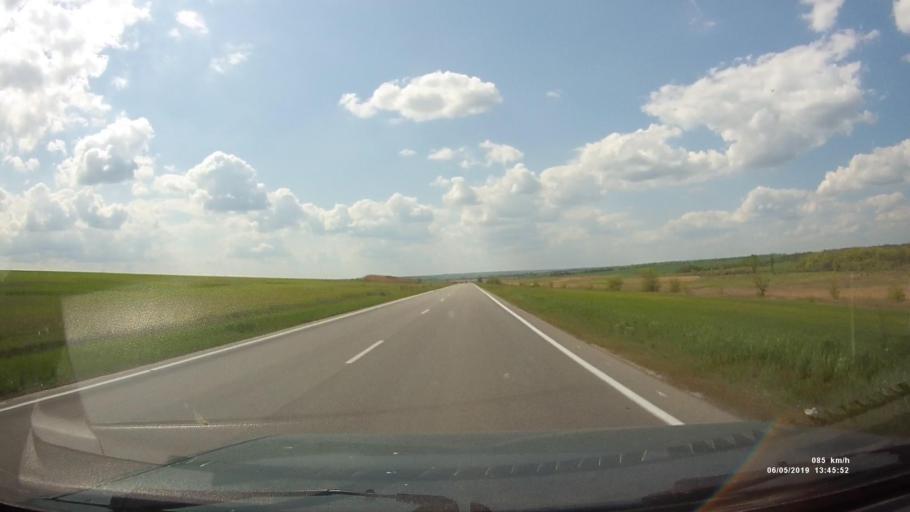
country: RU
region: Rostov
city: Melikhovskaya
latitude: 47.6575
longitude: 40.5924
